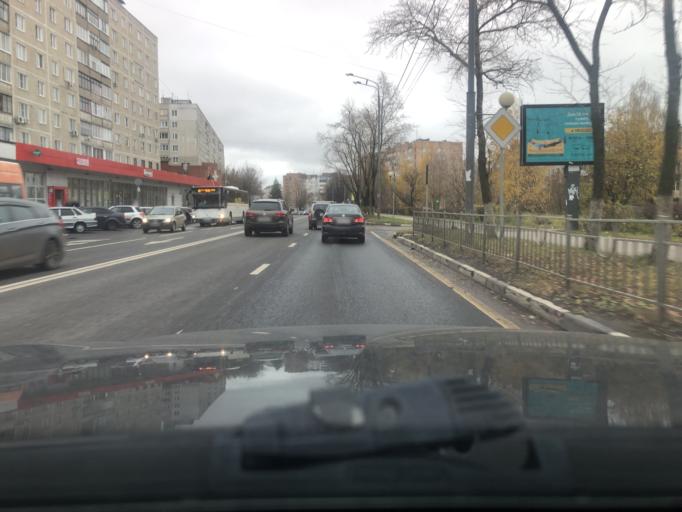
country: RU
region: Moskovskaya
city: Sergiyev Posad
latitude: 56.3292
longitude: 38.1318
